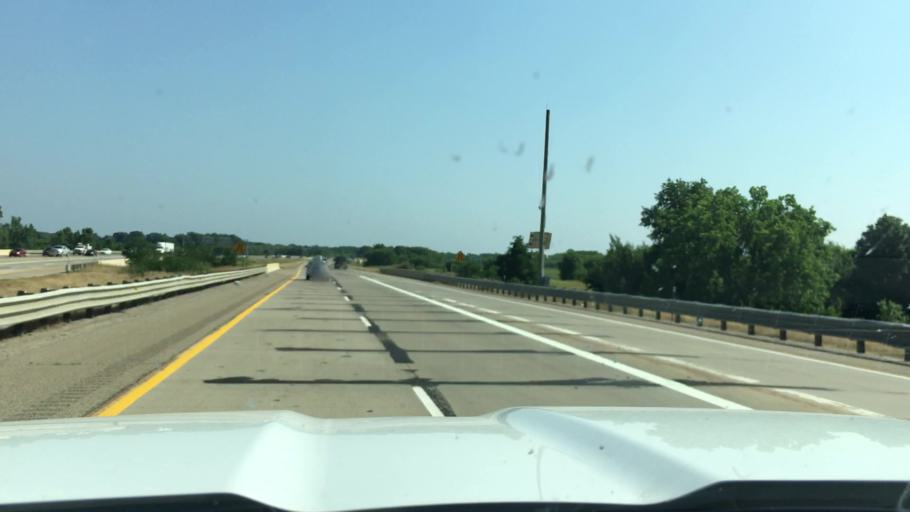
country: US
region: Michigan
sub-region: Kent County
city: Forest Hills
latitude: 42.8837
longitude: -85.4919
